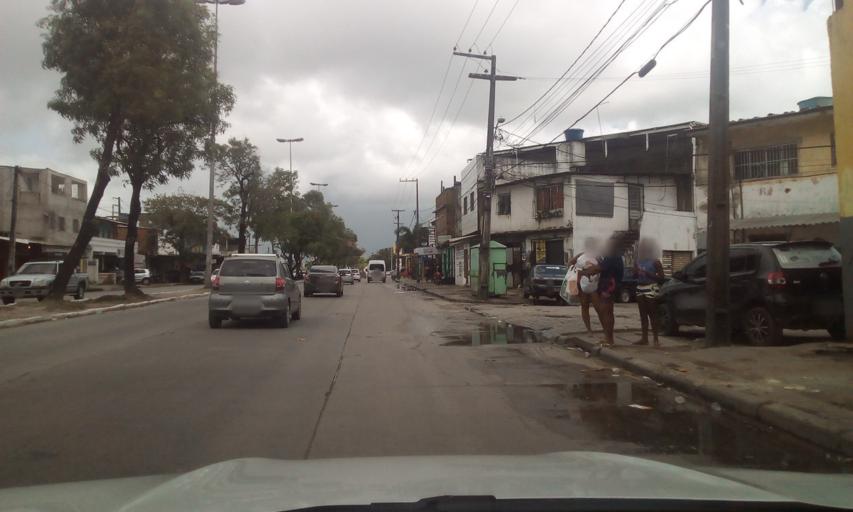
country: BR
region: Pernambuco
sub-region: Recife
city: Recife
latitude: -8.0641
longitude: -34.9359
